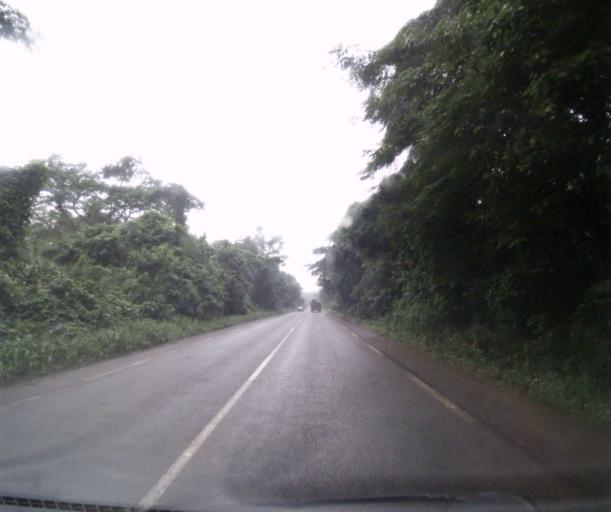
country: CM
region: Centre
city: Eseka
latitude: 3.8892
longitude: 10.7451
